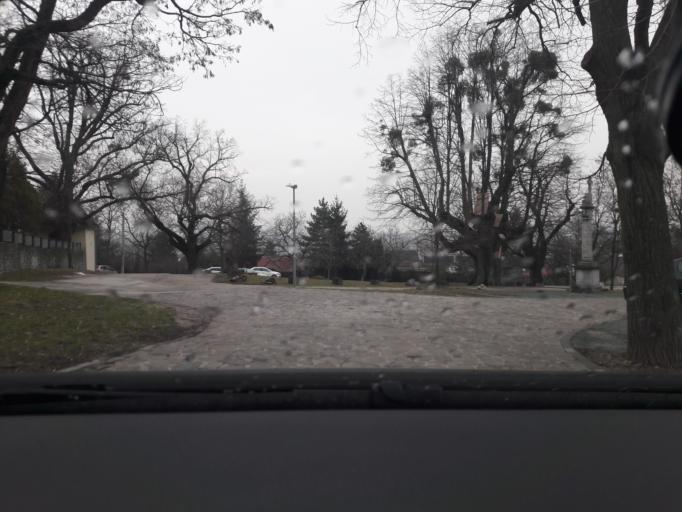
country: SK
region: Trnavsky
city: Smolenice
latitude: 48.5098
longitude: 17.4315
